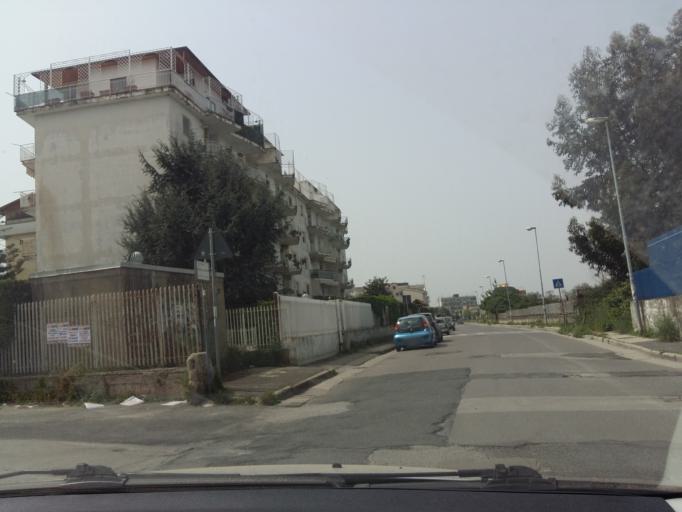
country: IT
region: Campania
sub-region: Provincia di Napoli
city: Mugnano di Napoli
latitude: 40.9007
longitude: 14.2002
